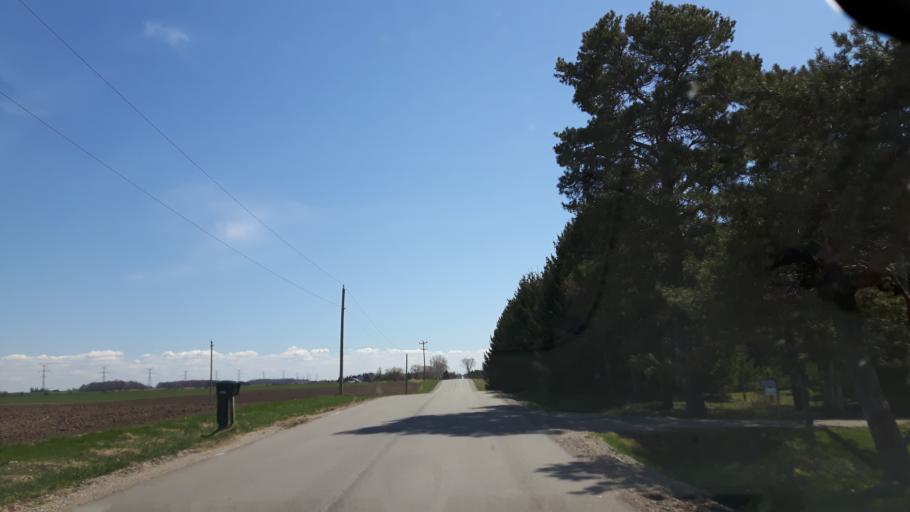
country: CA
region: Ontario
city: Goderich
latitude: 43.6212
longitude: -81.6440
